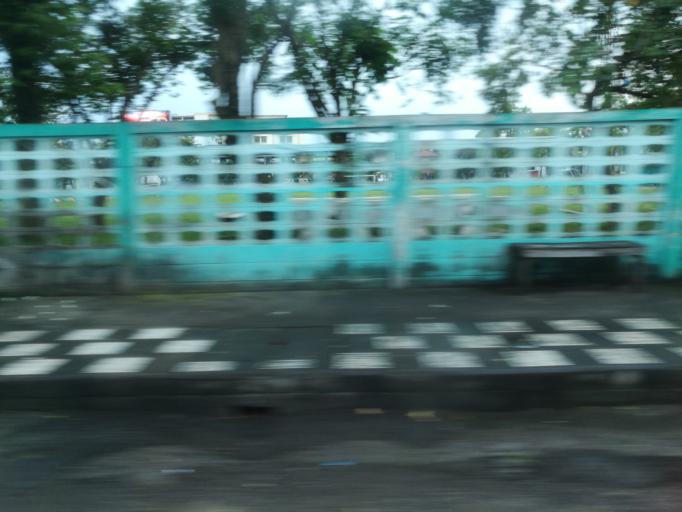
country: TH
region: Prachuap Khiri Khan
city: Prachuap Khiri Khan
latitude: 11.8039
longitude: 99.7972
